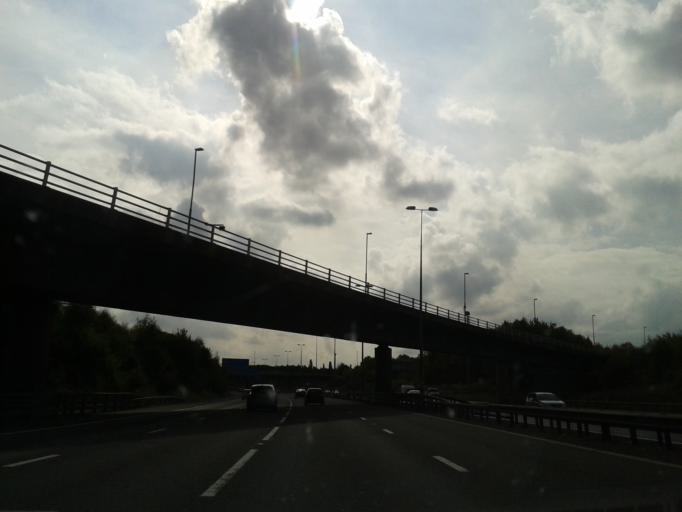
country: GB
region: England
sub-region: Warwickshire
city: Water Orton
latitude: 52.5111
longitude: -1.7256
